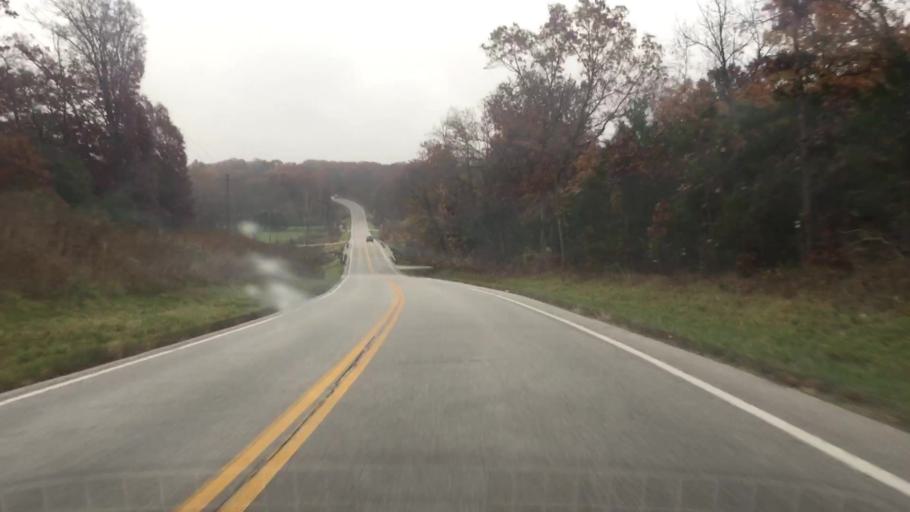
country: US
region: Missouri
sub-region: Callaway County
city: Fulton
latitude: 38.8830
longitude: -92.0929
